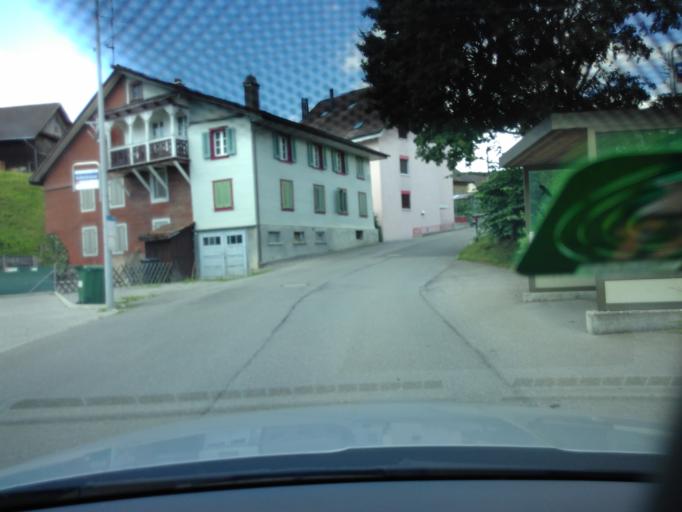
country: CH
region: Aargau
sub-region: Bezirk Muri
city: Oberruti
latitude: 47.1498
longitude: 8.3930
